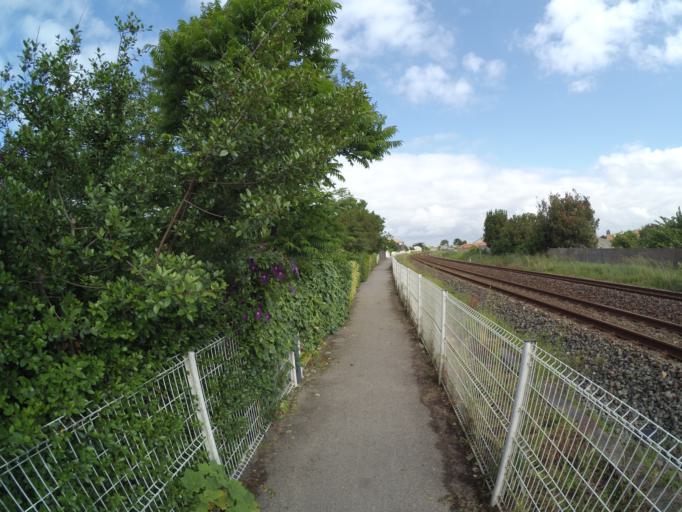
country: FR
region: Poitou-Charentes
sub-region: Departement de la Charente-Maritime
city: Angoulins
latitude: 46.1026
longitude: -1.1130
